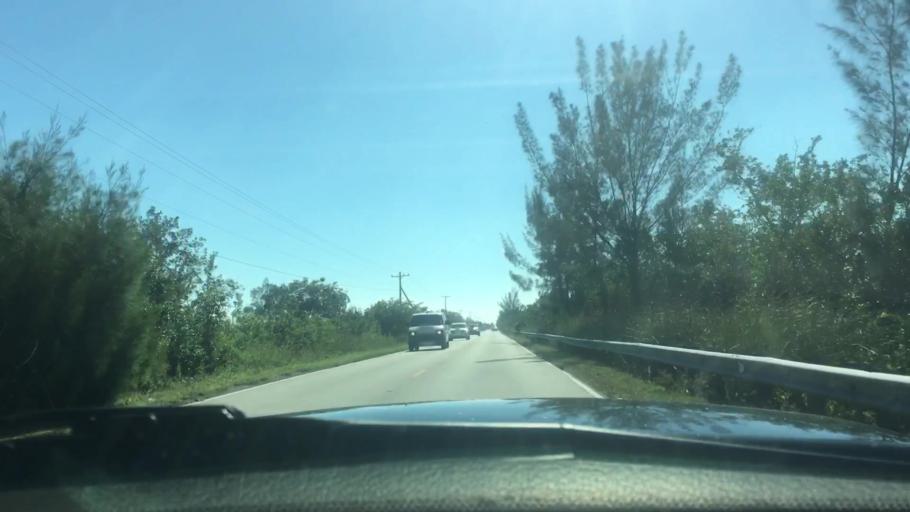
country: US
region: Florida
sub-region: Miami-Dade County
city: Florida City
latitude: 25.3621
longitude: -80.4267
